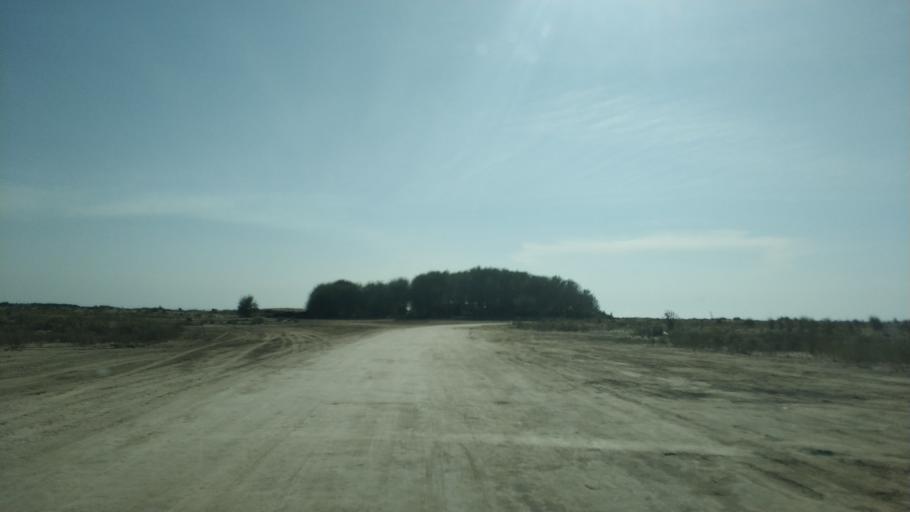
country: AL
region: Fier
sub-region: Rrethi i Lushnjes
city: Divjake
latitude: 40.9581
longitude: 19.4703
